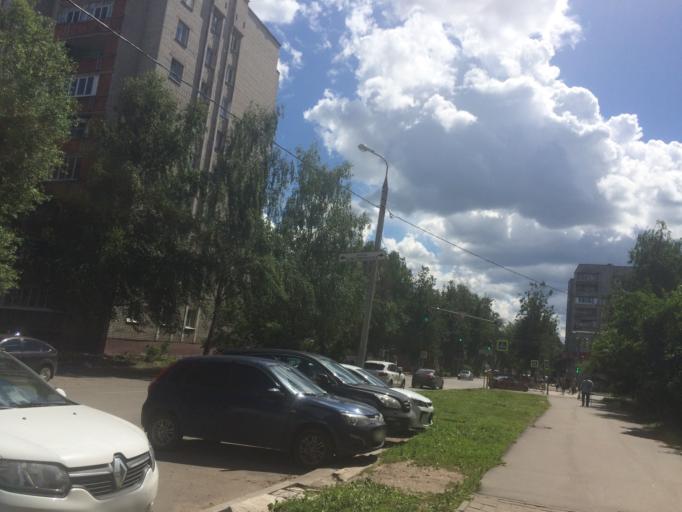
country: RU
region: Jaroslavl
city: Yaroslavl
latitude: 57.6218
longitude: 39.8623
